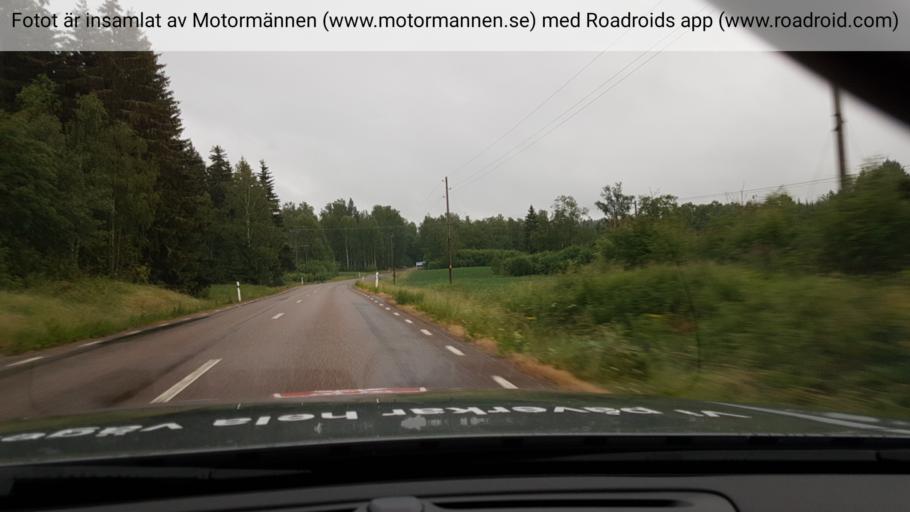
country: SE
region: Vaestmanland
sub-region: Norbergs Kommun
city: Norberg
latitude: 60.0214
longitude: 16.0273
